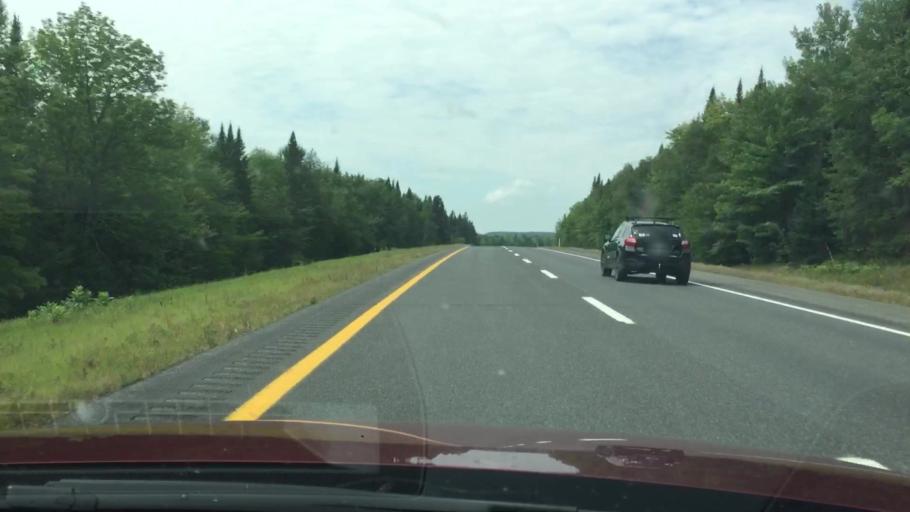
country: US
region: Maine
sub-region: Aroostook County
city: Hodgdon
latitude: 46.1408
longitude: -68.0193
